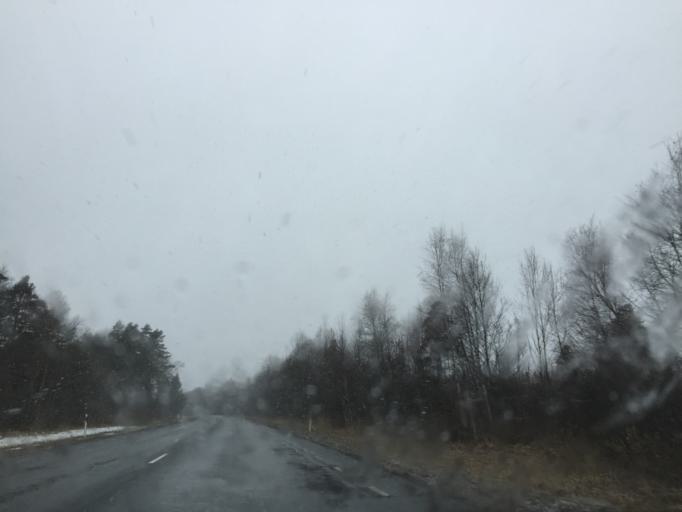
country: EE
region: Laeaene
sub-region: Ridala Parish
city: Uuemoisa
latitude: 58.8311
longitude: 23.7008
